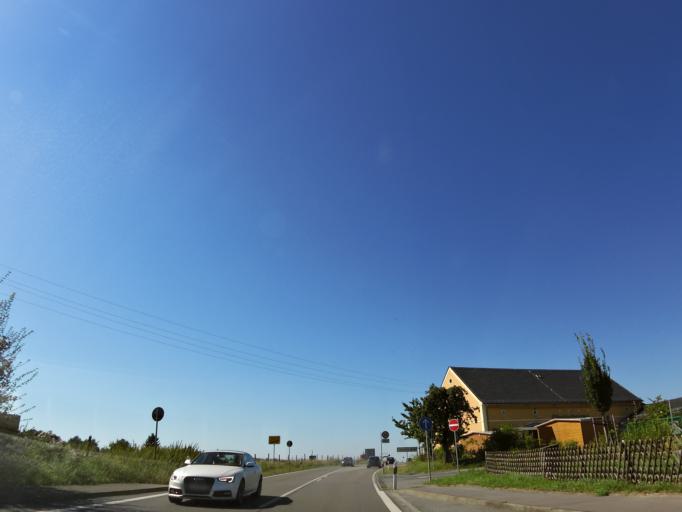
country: DE
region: Saxony
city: Struppen
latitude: 50.9292
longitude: 13.9782
